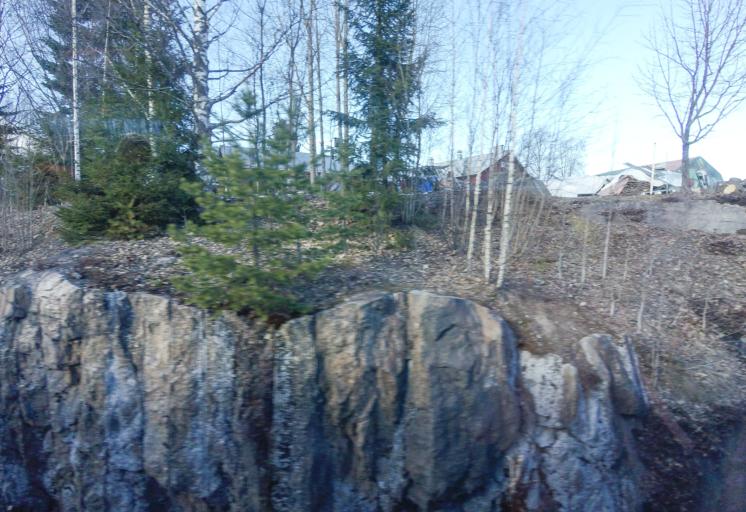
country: FI
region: South Karelia
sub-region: Imatra
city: Simpele
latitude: 61.4246
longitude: 29.3888
